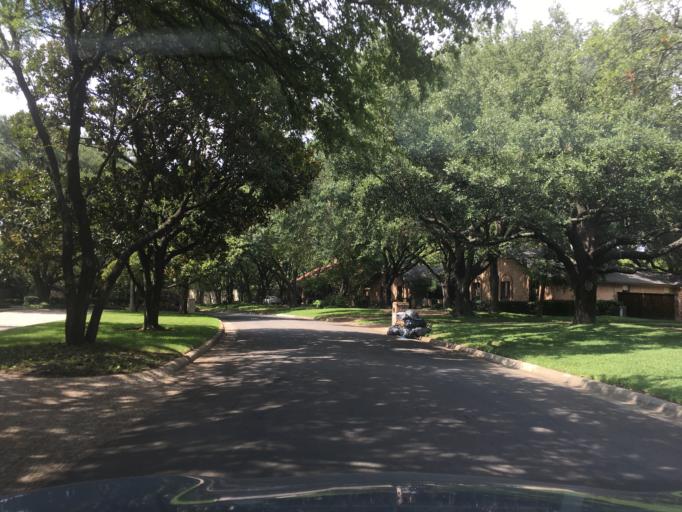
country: US
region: Texas
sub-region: Dallas County
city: University Park
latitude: 32.8964
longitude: -96.8227
